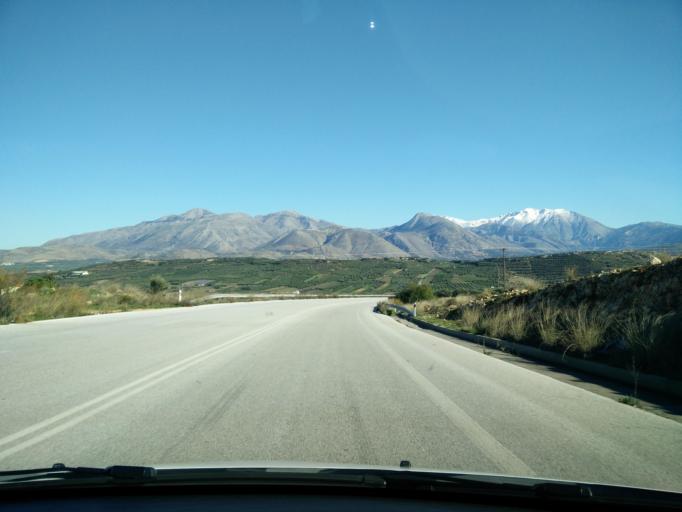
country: GR
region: Crete
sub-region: Nomos Irakleiou
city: Arkalochori
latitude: 35.1351
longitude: 25.2708
